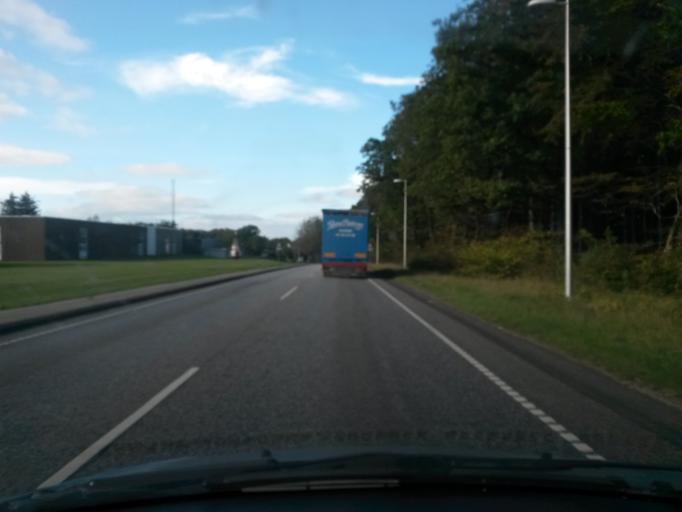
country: DK
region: Central Jutland
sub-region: Holstebro Kommune
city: Holstebro
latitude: 56.3421
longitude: 8.6372
